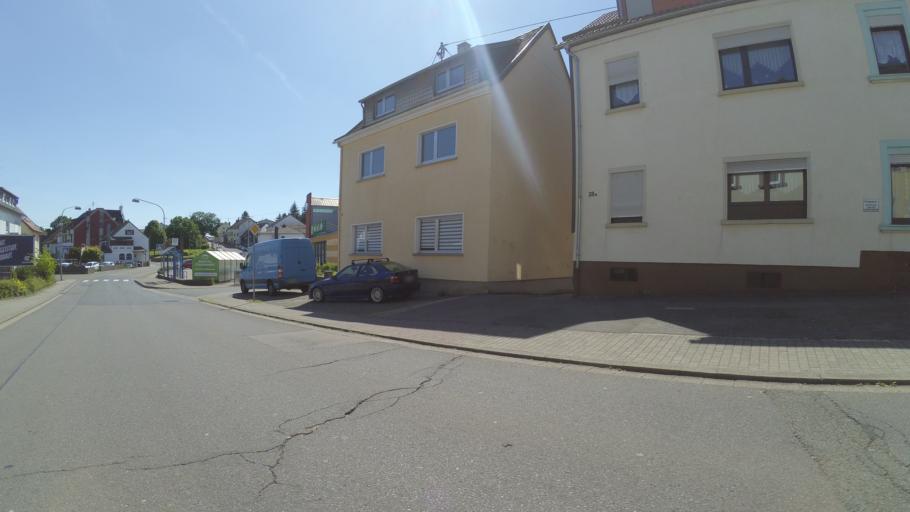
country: DE
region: Saarland
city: Quierschied
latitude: 49.3226
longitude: 7.0547
